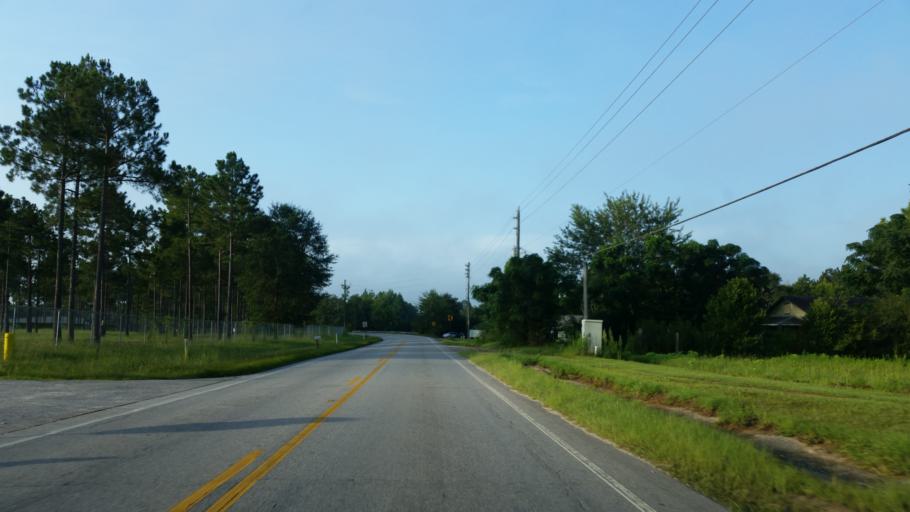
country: US
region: Florida
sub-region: Escambia County
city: Cantonment
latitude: 30.6538
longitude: -87.3222
